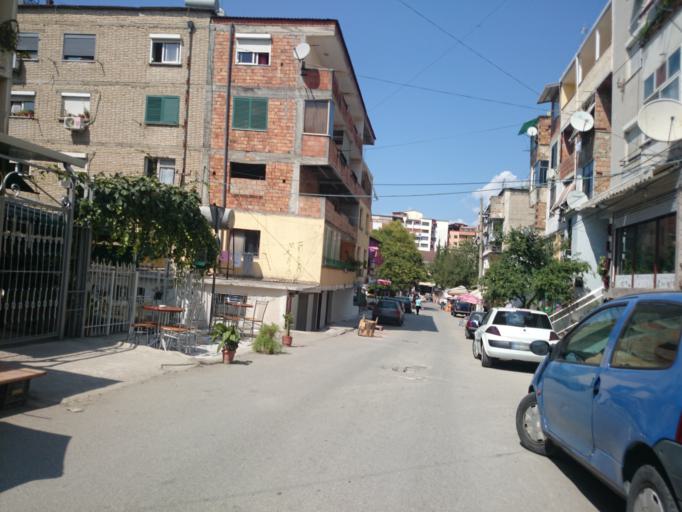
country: AL
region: Tirane
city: Tirana
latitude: 41.3243
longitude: 19.8290
